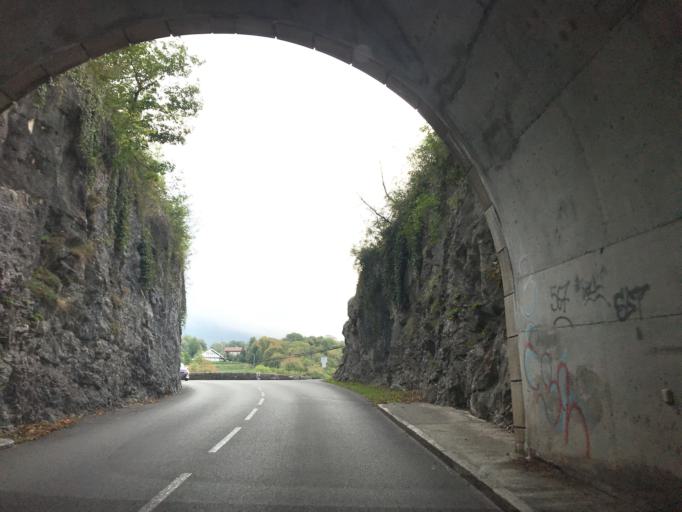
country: FR
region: Rhone-Alpes
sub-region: Departement de la Haute-Savoie
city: Talloires
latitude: 45.8425
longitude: 6.2217
